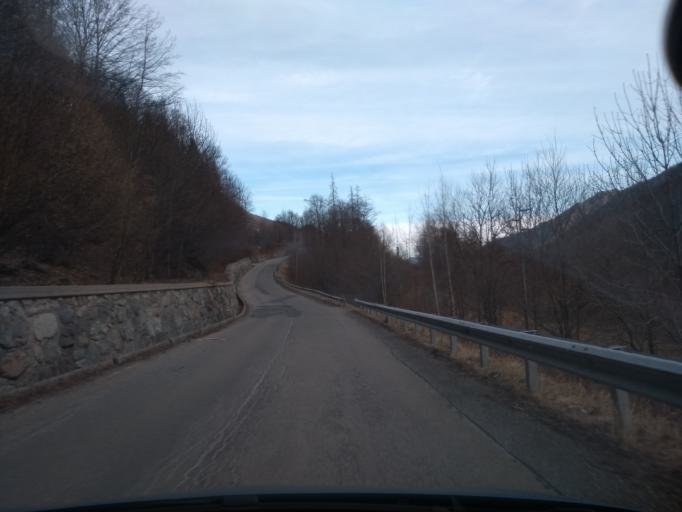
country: IT
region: Piedmont
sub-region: Provincia di Torino
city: Ala di Stura
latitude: 45.3122
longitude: 7.2677
